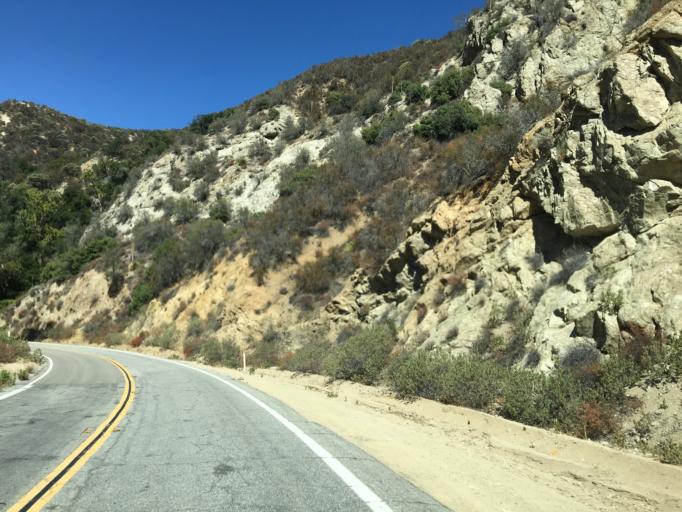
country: US
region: California
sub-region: Los Angeles County
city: Green Valley
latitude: 34.6301
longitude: -118.5440
